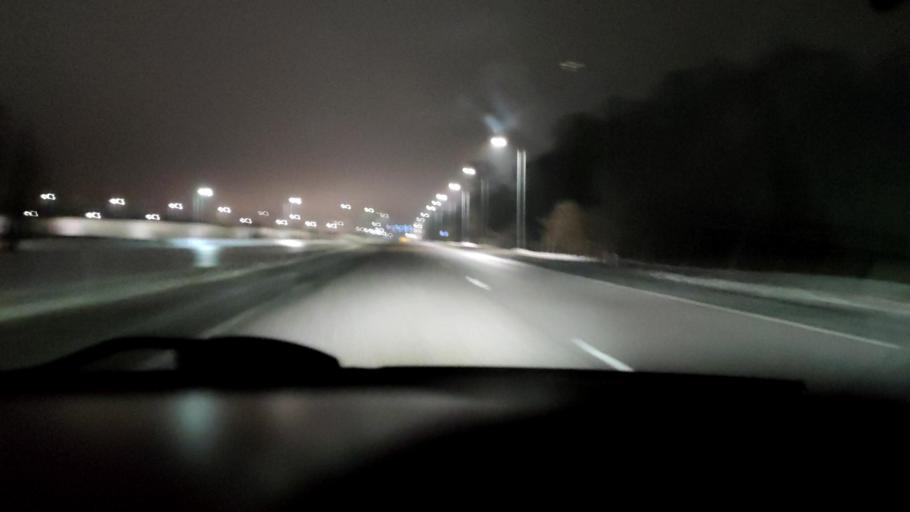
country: RU
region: Voronezj
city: Podgornoye
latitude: 51.8400
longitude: 39.2139
